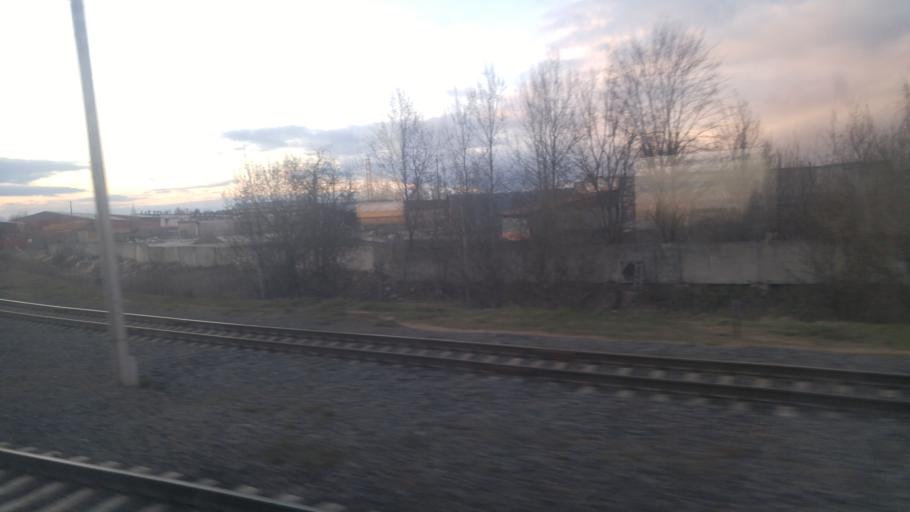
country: BY
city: Michanovichi
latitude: 53.7532
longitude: 27.6793
